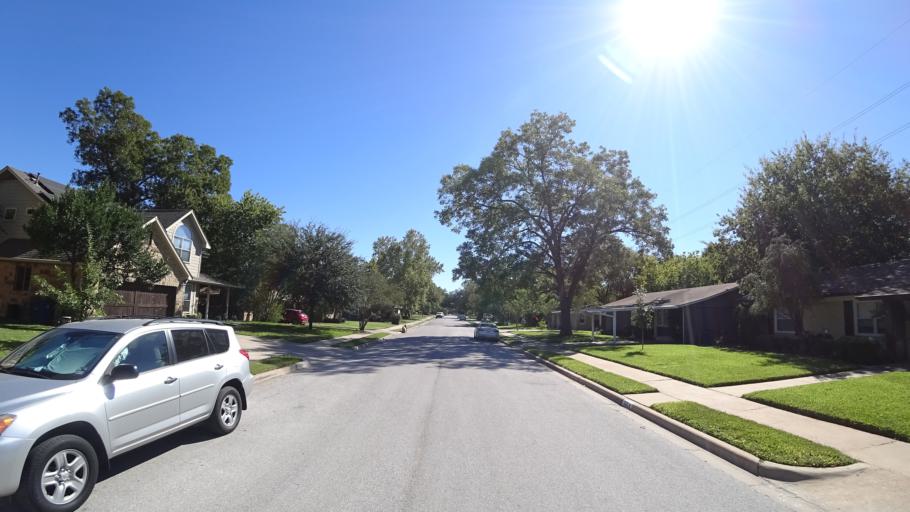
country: US
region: Texas
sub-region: Travis County
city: West Lake Hills
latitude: 30.3296
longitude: -97.7549
